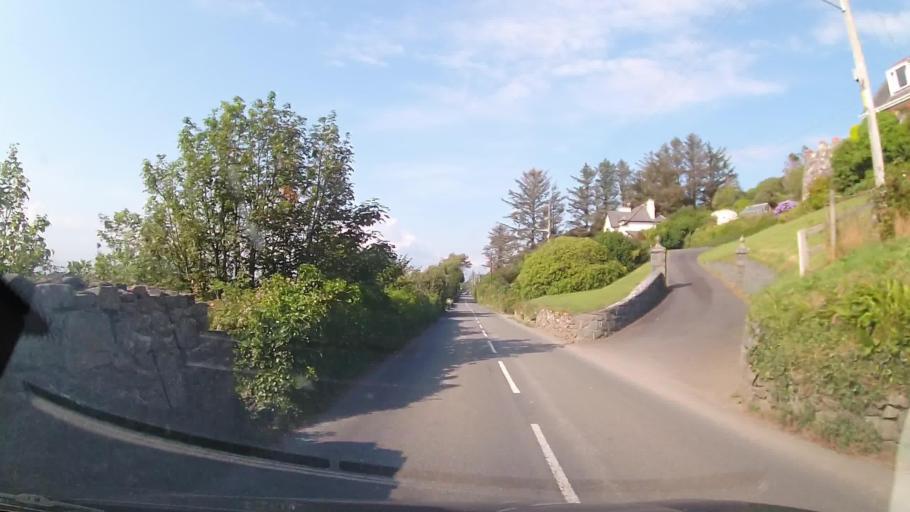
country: GB
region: Wales
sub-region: Gwynedd
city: Llanfair
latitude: 52.8481
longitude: -4.1159
